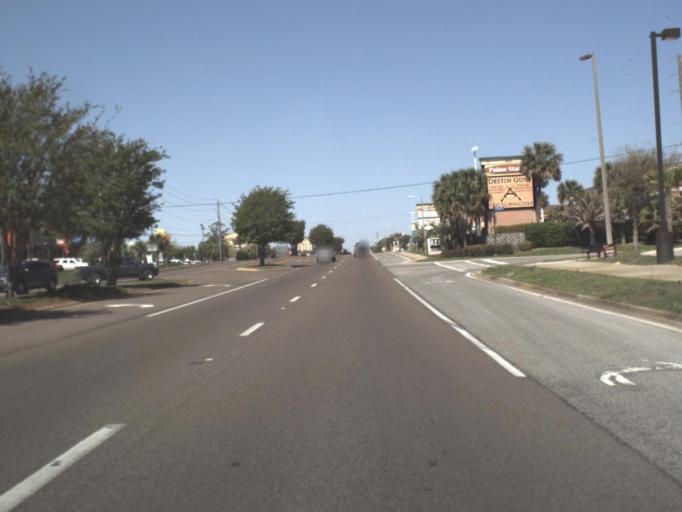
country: US
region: Florida
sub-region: Okaloosa County
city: Destin
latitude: 30.3879
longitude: -86.4753
